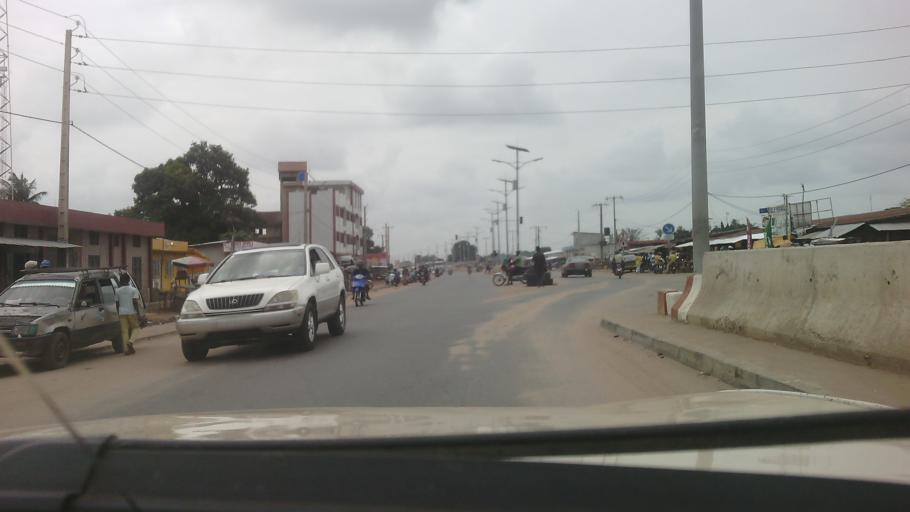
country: BJ
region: Atlantique
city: Hevie
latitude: 6.3854
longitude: 2.2089
